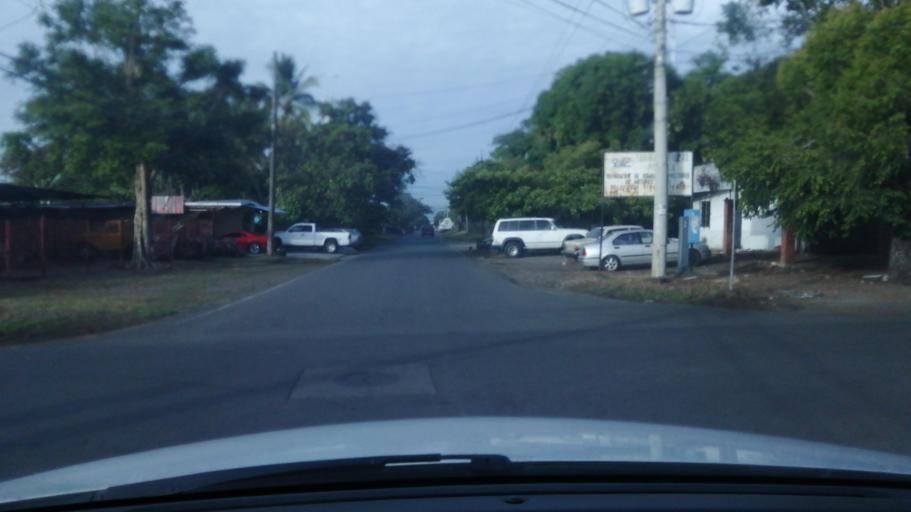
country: PA
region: Chiriqui
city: David
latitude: 8.4394
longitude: -82.4347
